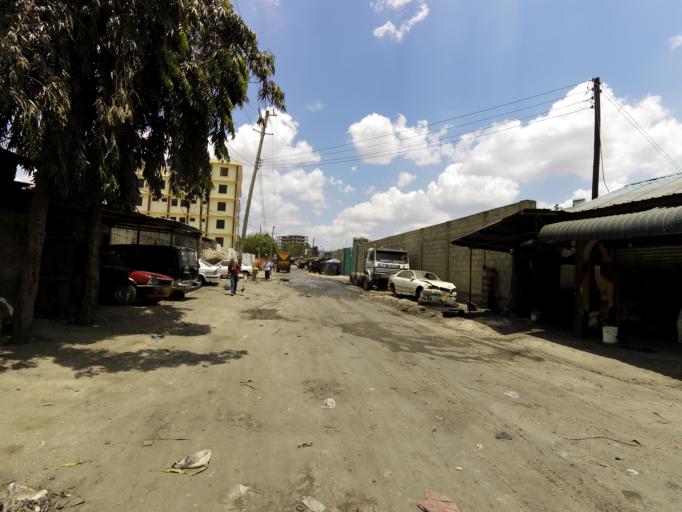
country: TZ
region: Dar es Salaam
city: Dar es Salaam
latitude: -6.8348
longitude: 39.2443
